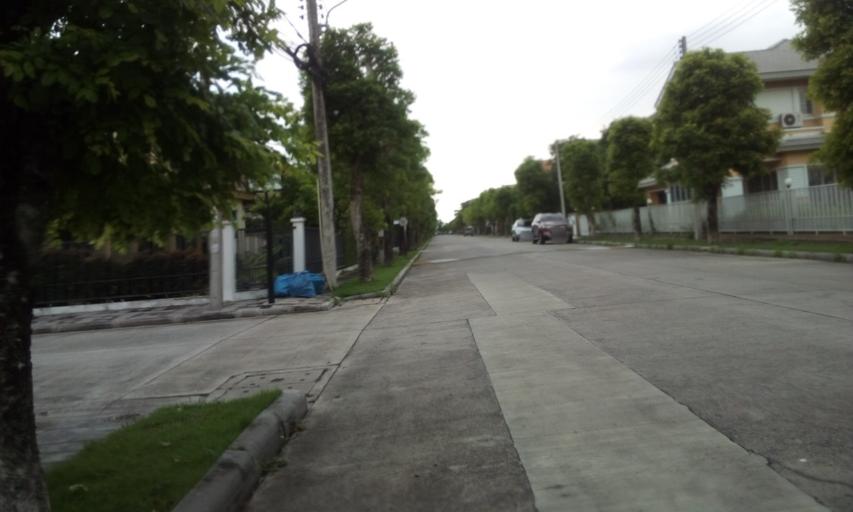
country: TH
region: Pathum Thani
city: Ban Rangsit
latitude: 14.0468
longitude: 100.8286
